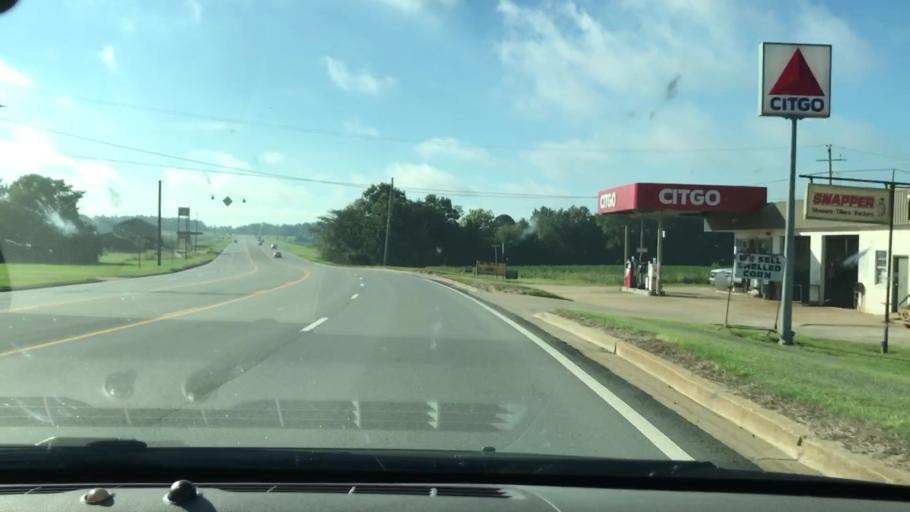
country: US
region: Georgia
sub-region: Terrell County
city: Dawson
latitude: 31.7188
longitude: -84.3484
